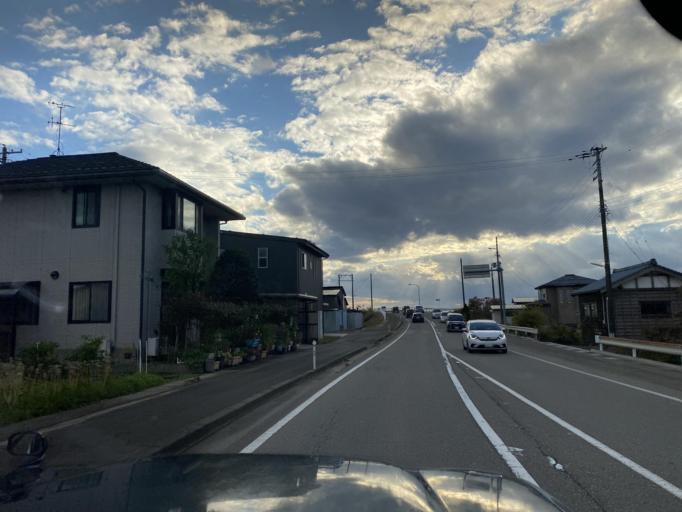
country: JP
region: Niigata
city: Kamo
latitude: 37.6733
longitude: 139.0126
